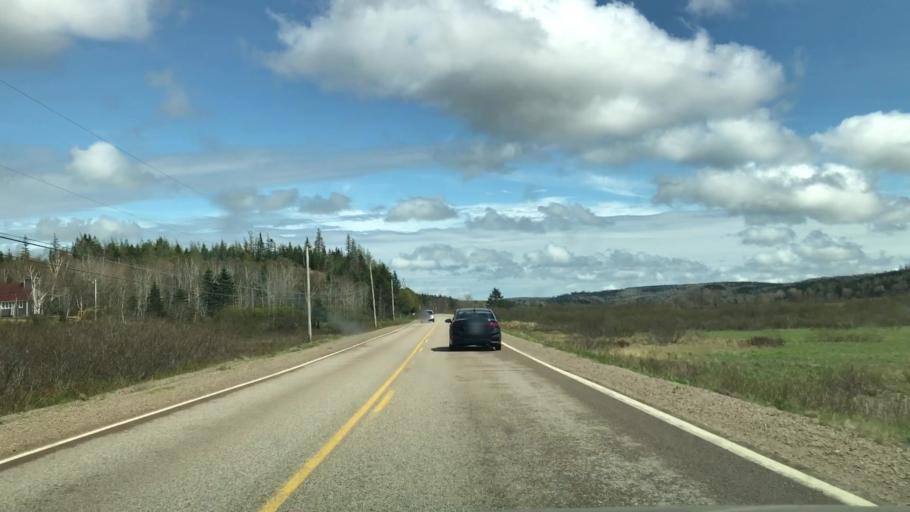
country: CA
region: Nova Scotia
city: Antigonish
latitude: 45.1952
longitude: -61.9995
